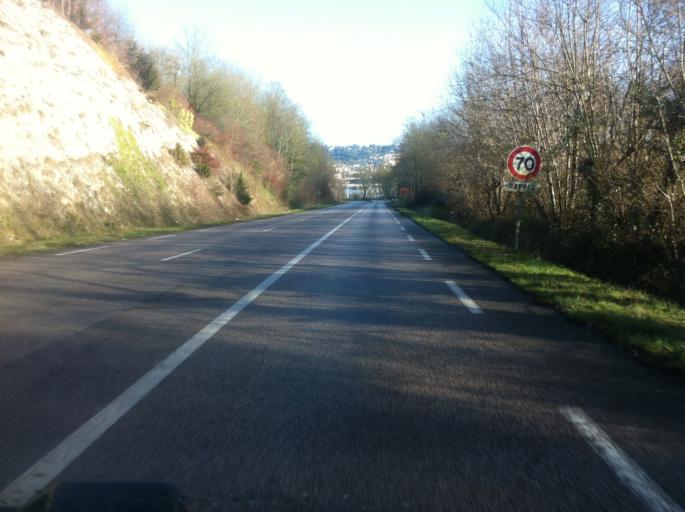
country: FR
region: Haute-Normandie
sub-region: Departement de la Seine-Maritime
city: Canteleu
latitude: 49.4436
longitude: 1.0383
